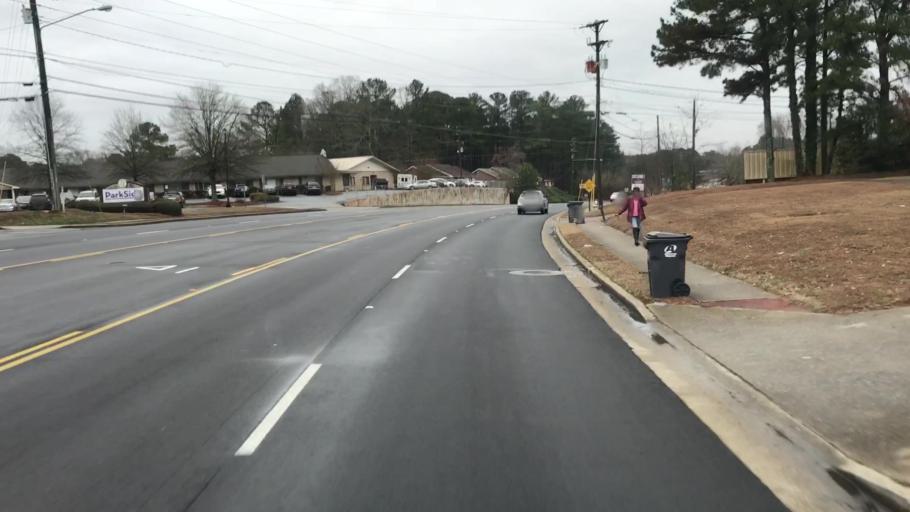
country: US
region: Georgia
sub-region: Gwinnett County
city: Snellville
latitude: 33.8380
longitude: -84.0087
